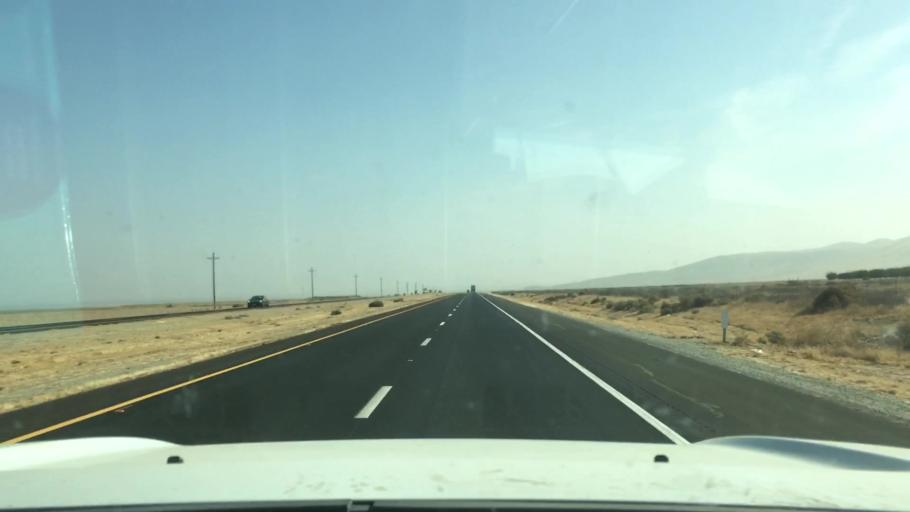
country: US
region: California
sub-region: San Luis Obispo County
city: Shandon
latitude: 35.6696
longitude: -120.0793
